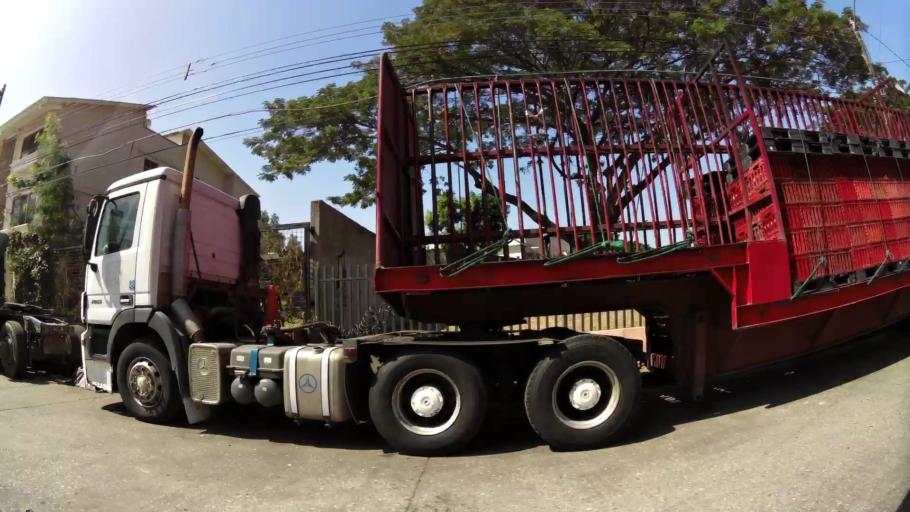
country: EC
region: Guayas
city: Eloy Alfaro
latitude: -2.1337
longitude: -79.9101
